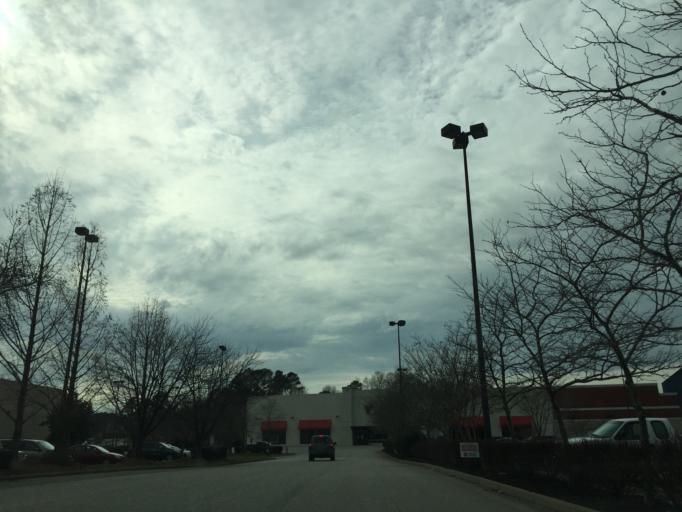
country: US
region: Virginia
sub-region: York County
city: Yorktown
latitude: 37.1079
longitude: -76.4970
